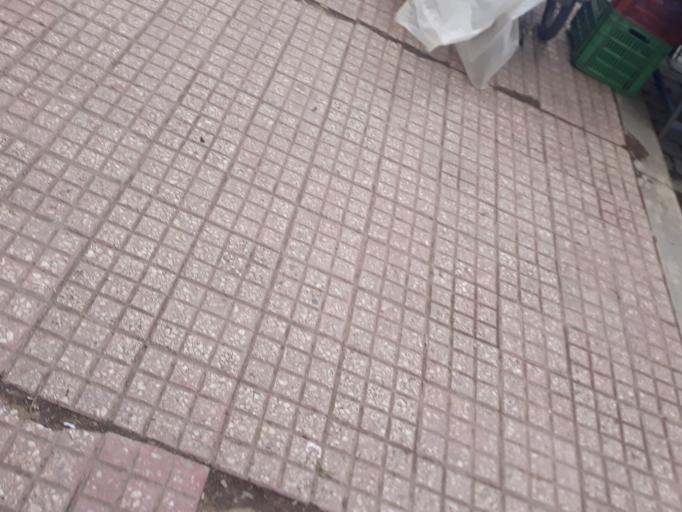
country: BO
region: La Paz
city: Achacachi
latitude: -16.0443
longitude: -68.6850
